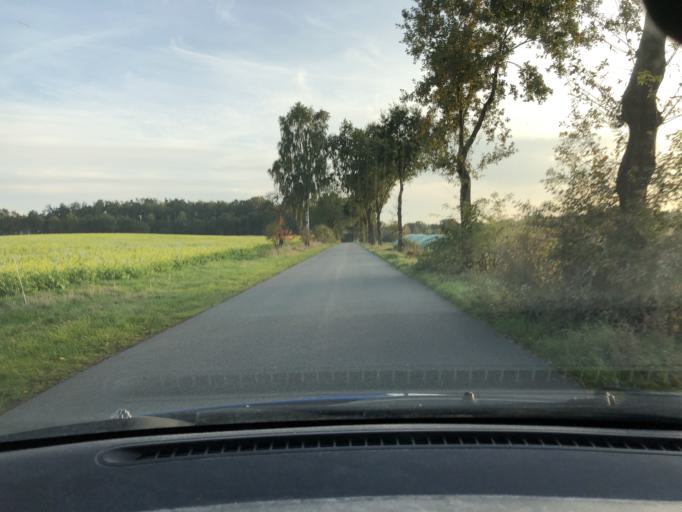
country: DE
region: Lower Saxony
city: Gohrde
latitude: 53.1277
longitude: 10.9455
